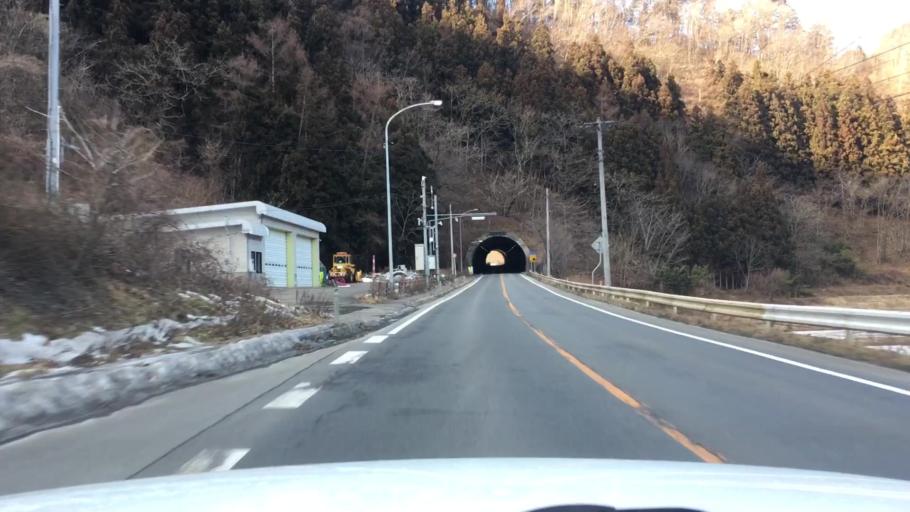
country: JP
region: Iwate
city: Tono
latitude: 39.6242
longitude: 141.6107
